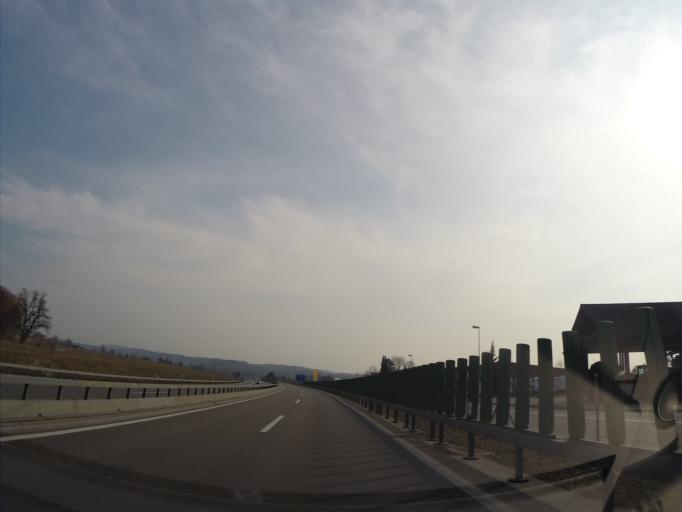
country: CH
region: Zurich
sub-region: Bezirk Andelfingen
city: Kleinandelfingen
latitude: 47.6072
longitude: 8.6870
